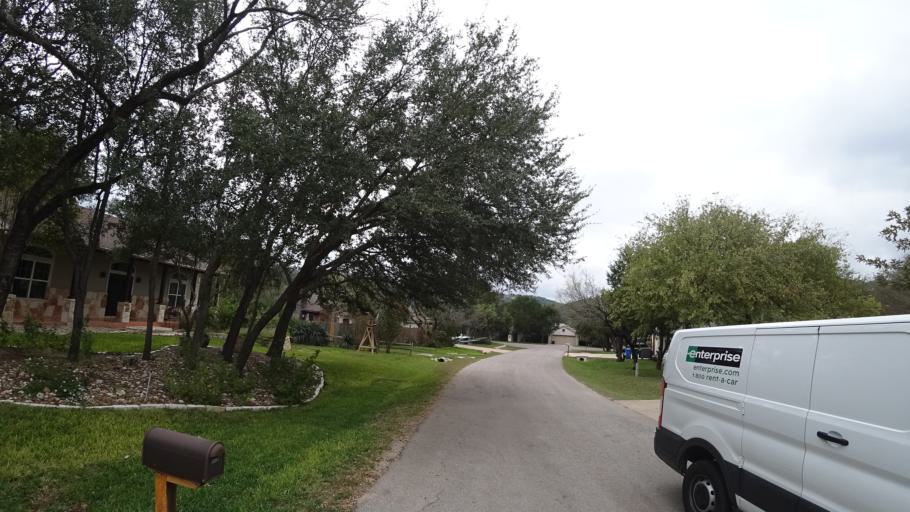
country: US
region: Texas
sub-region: Travis County
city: Bee Cave
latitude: 30.3304
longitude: -97.9221
